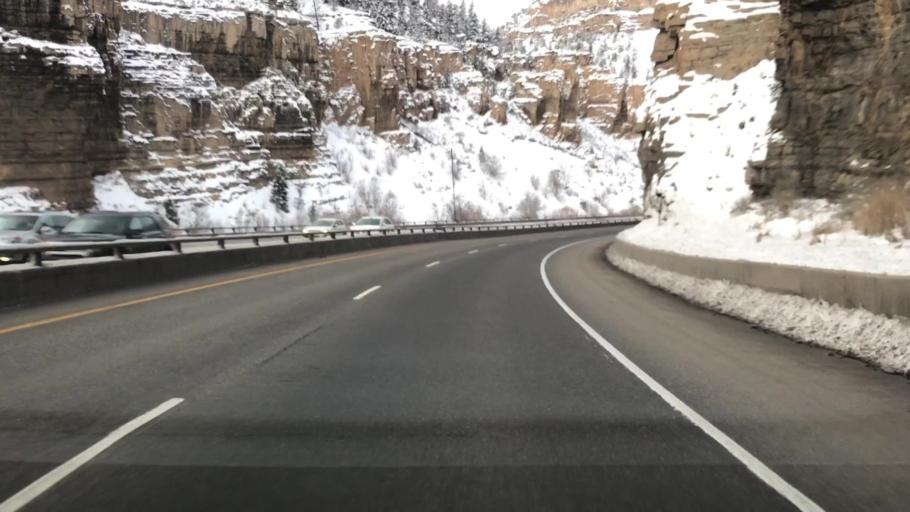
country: US
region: Colorado
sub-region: Eagle County
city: Gypsum
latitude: 39.6243
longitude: -107.1163
